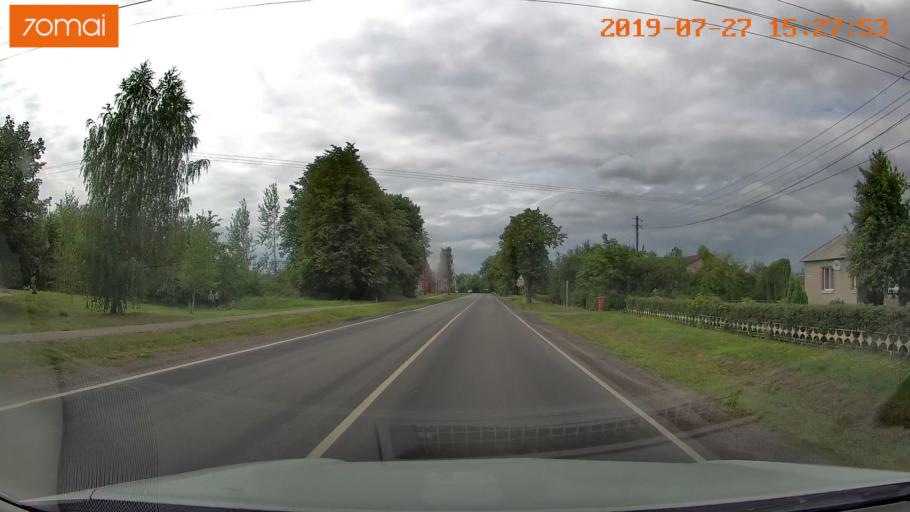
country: RU
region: Kaliningrad
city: Nesterov
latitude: 54.6336
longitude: 22.5574
